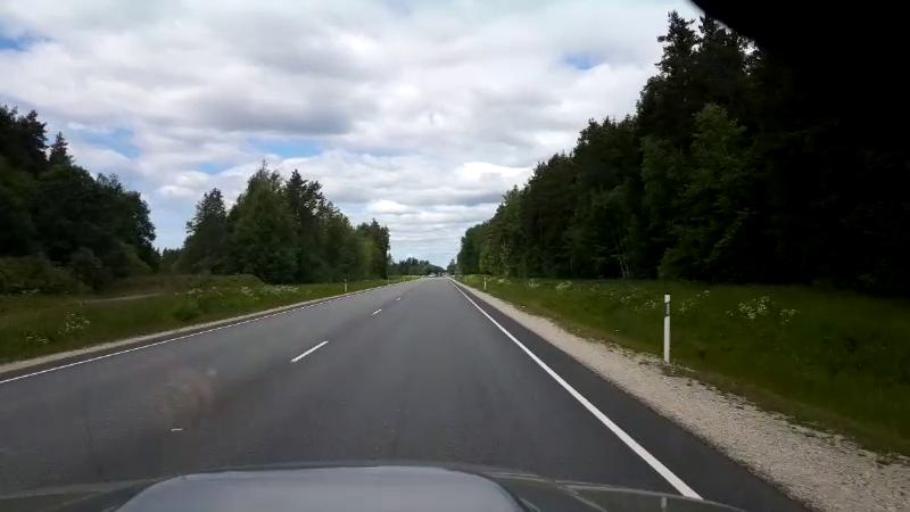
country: EE
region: Raplamaa
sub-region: Maerjamaa vald
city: Marjamaa
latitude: 58.8022
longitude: 24.4128
